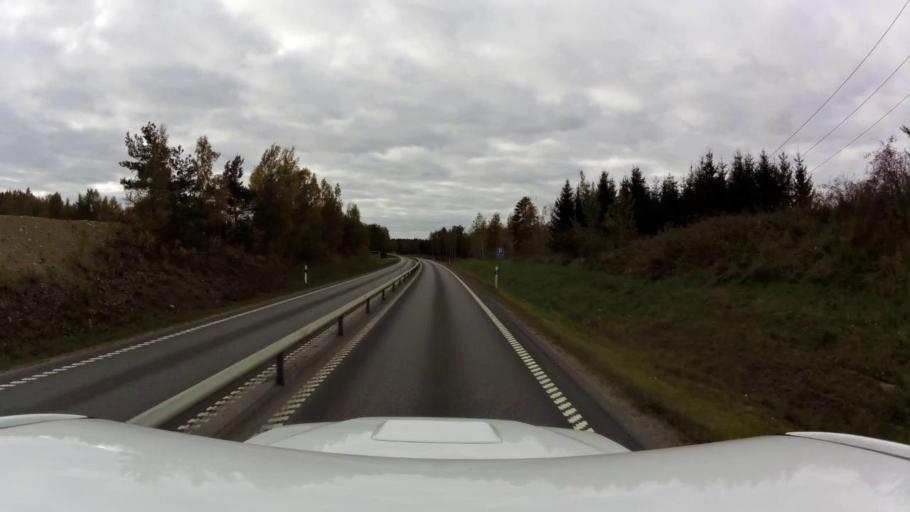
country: SE
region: OEstergoetland
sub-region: Linkopings Kommun
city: Malmslatt
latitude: 58.3888
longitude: 15.5430
